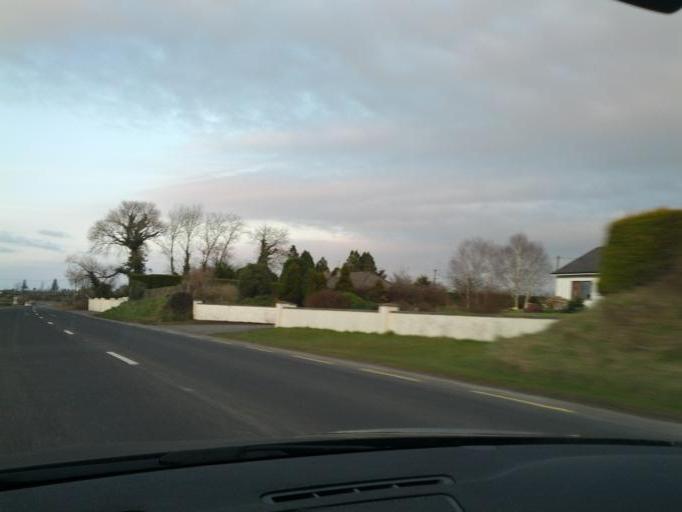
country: IE
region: Munster
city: Nenagh Bridge
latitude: 52.9109
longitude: -8.1799
